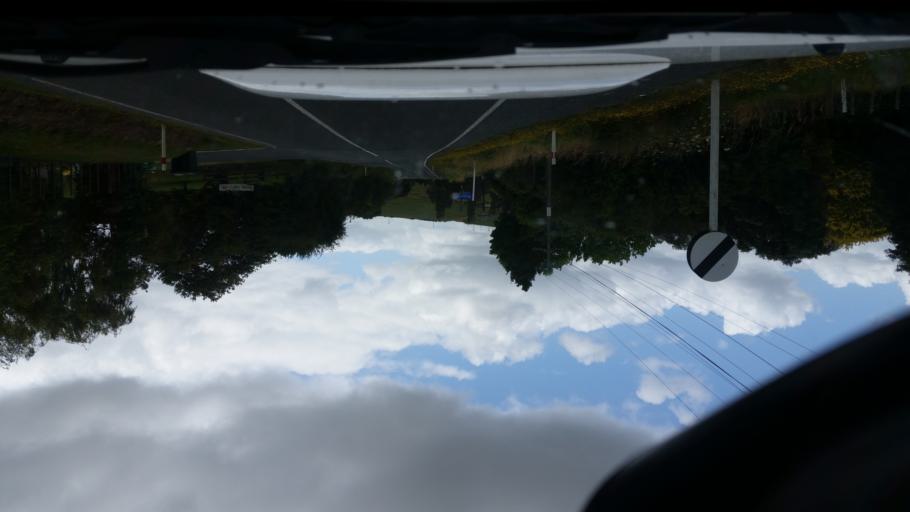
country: NZ
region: Northland
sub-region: Whangarei
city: Ruakaka
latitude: -36.0976
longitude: 174.3509
